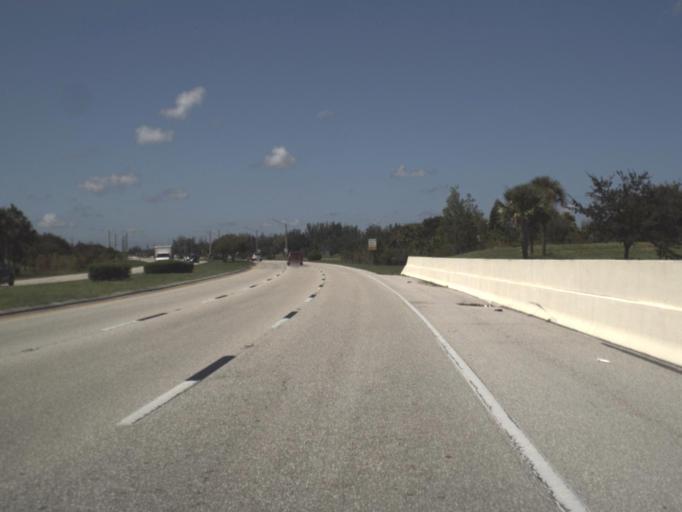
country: US
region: Florida
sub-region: Lee County
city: Cape Coral
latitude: 26.6068
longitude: -81.9857
